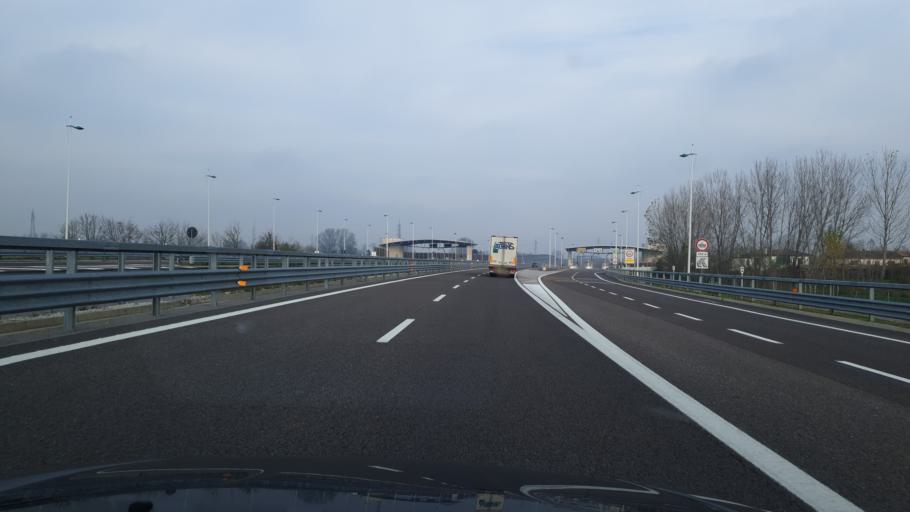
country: IT
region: Veneto
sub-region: Provincia di Padova
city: Santa Margherita d'Adige
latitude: 45.2099
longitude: 11.5432
